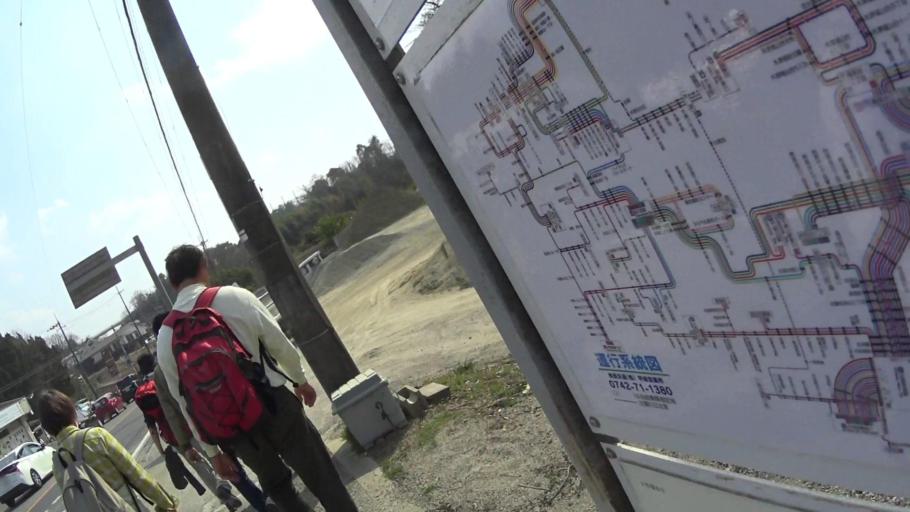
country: JP
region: Nara
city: Nara-shi
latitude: 34.7058
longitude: 135.8272
